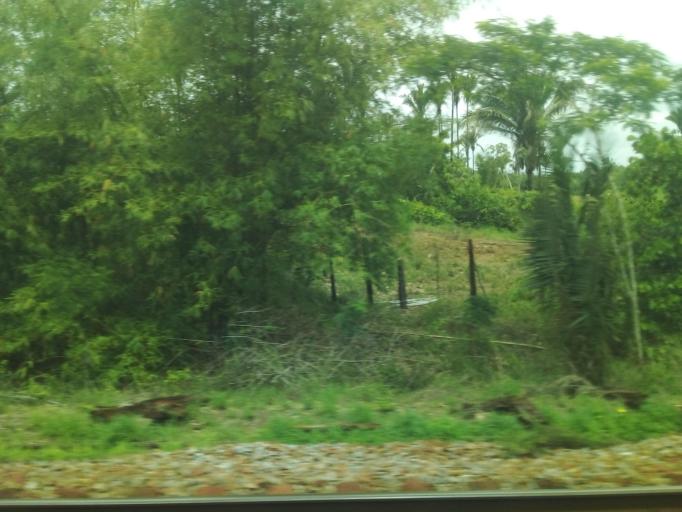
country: BR
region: Maranhao
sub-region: Vitoria Do Mearim
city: Vitoria do Mearim
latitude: -3.5380
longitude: -44.8844
